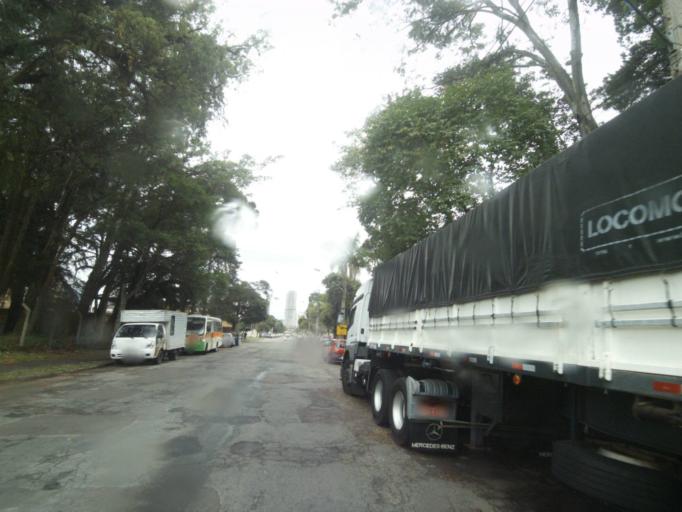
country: BR
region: Parana
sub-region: Curitiba
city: Curitiba
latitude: -25.4463
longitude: -49.3479
